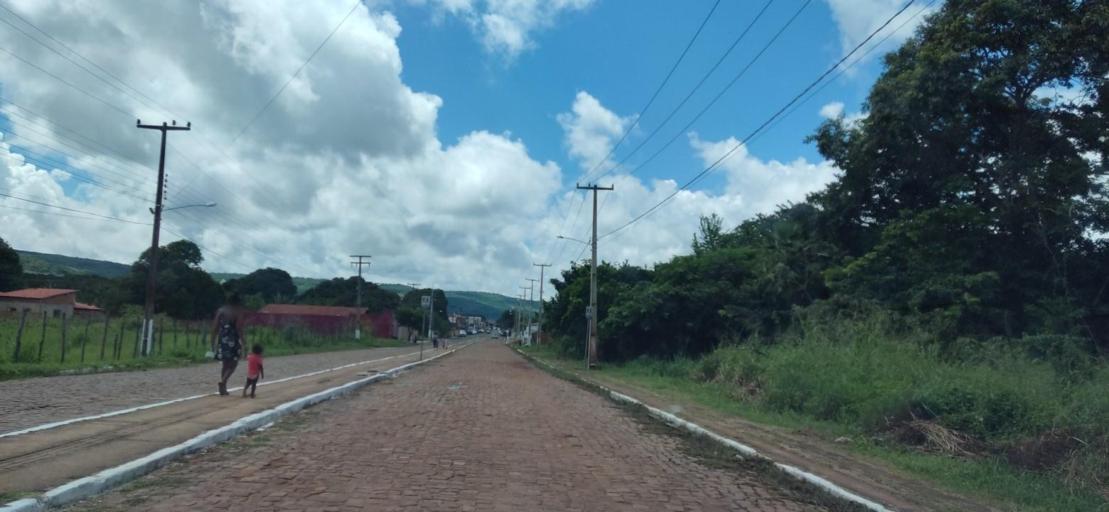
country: BR
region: Piaui
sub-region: Valenca Do Piaui
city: Valenca do Piaui
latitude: -6.1111
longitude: -41.7942
